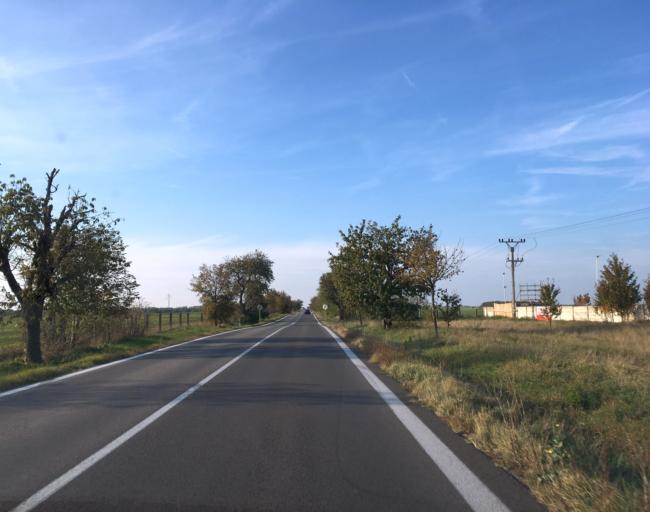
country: SK
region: Nitriansky
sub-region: Okres Nove Zamky
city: Nove Zamky
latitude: 48.0170
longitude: 18.1492
